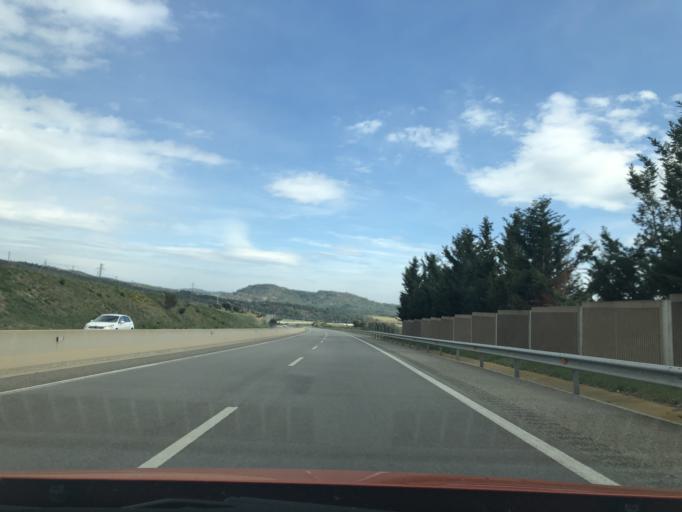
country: ES
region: Catalonia
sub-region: Provincia de Barcelona
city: Avia
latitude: 42.0824
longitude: 1.8611
